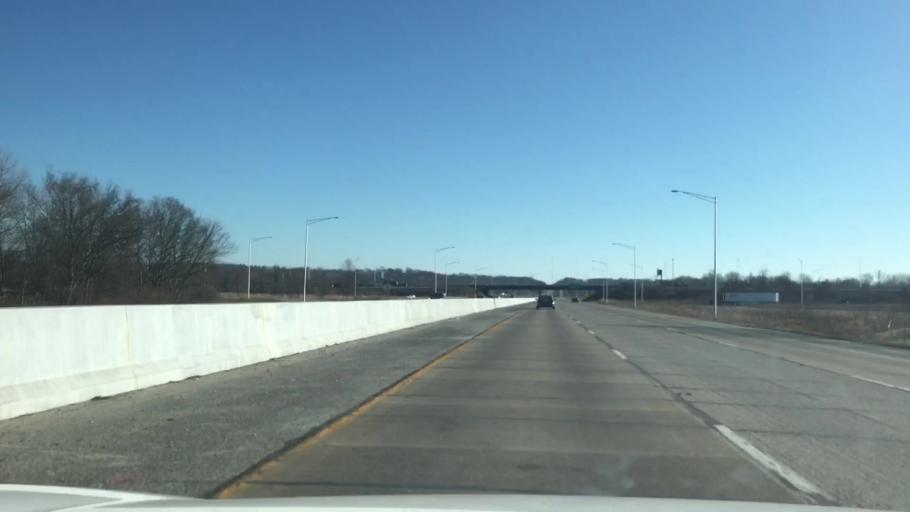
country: US
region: Illinois
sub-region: Saint Clair County
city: Alorton
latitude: 38.5857
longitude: -90.1114
